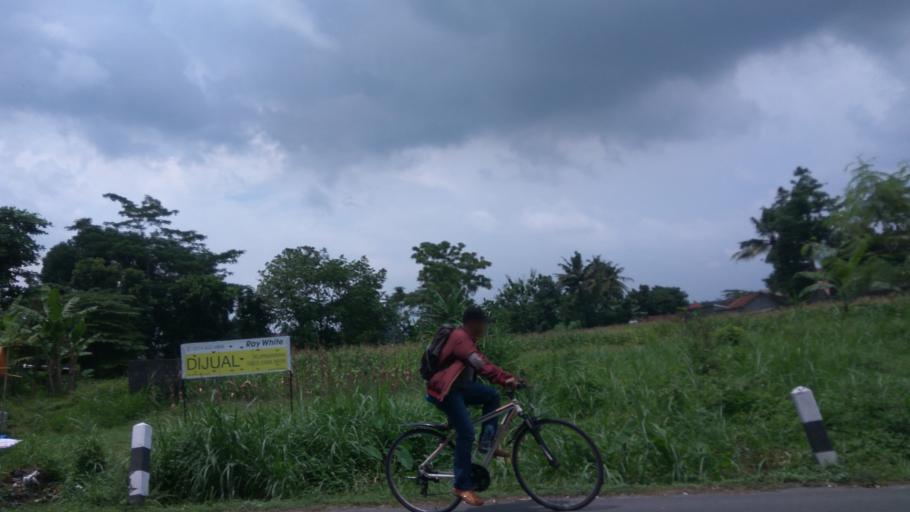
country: ID
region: Daerah Istimewa Yogyakarta
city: Melati
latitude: -7.7257
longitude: 110.4004
